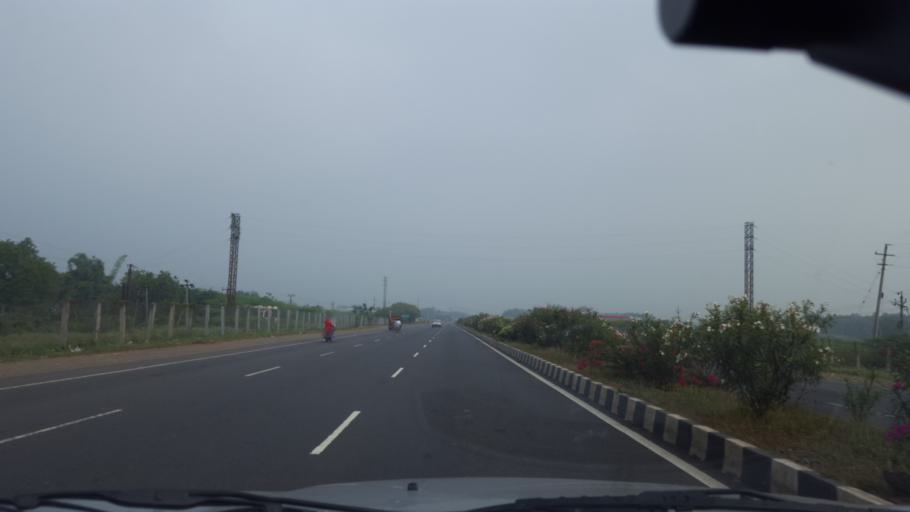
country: IN
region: Andhra Pradesh
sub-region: Prakasam
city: Ongole
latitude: 15.6458
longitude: 80.0155
